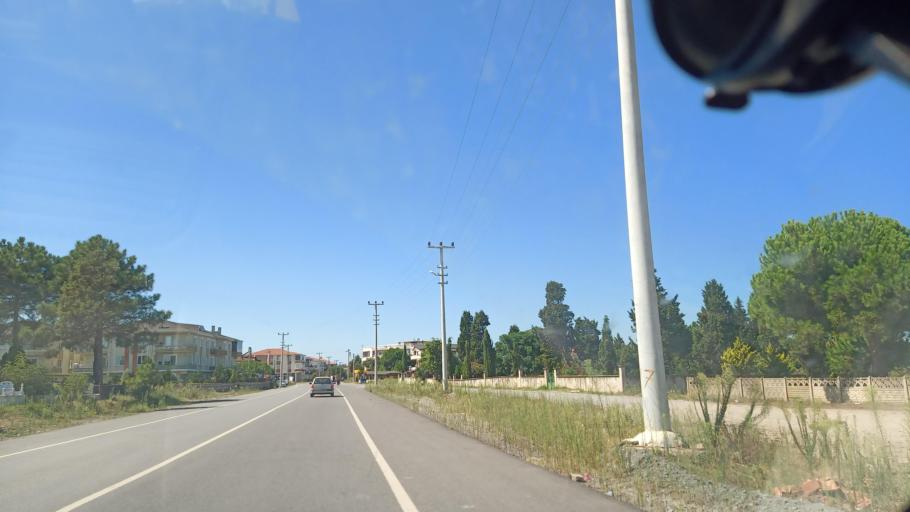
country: TR
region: Sakarya
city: Karasu
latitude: 41.1193
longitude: 30.6566
